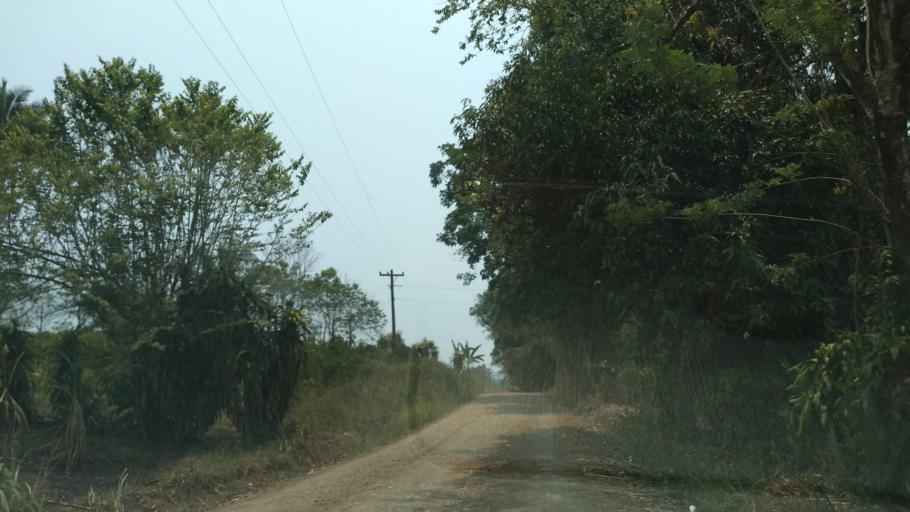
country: MX
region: Veracruz
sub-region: Tezonapa
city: Laguna Chica (Pueblo Nuevo)
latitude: 18.5031
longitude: -96.7726
